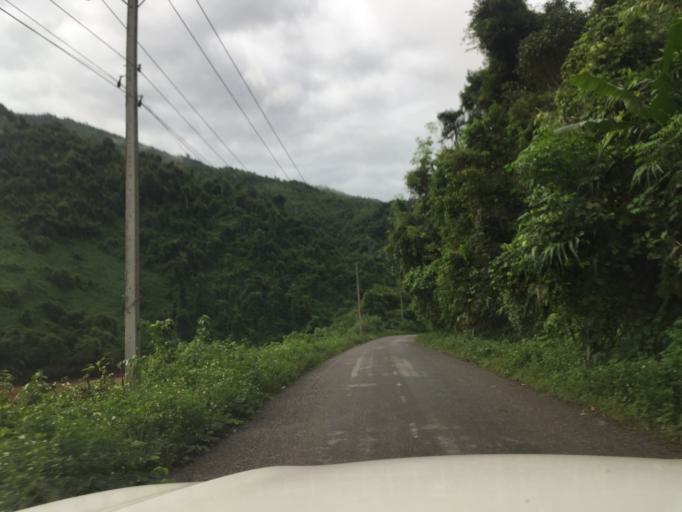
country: LA
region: Oudomxai
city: Muang La
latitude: 21.0599
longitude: 102.2410
